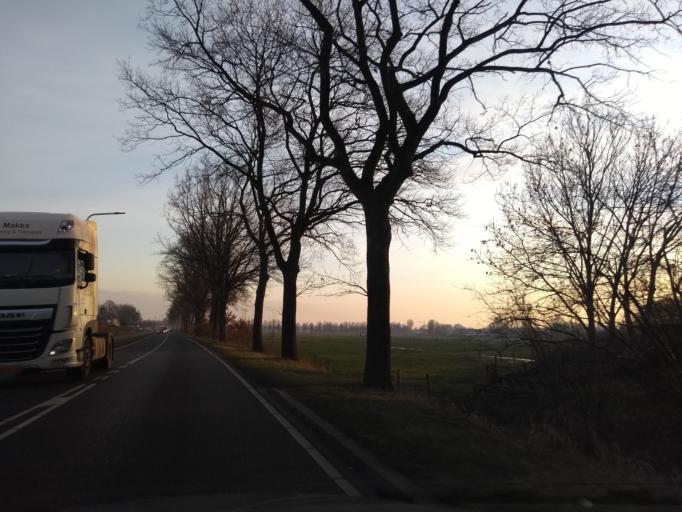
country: NL
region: Overijssel
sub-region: Gemeente Twenterand
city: Vriezenveen
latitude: 52.4024
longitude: 6.6066
